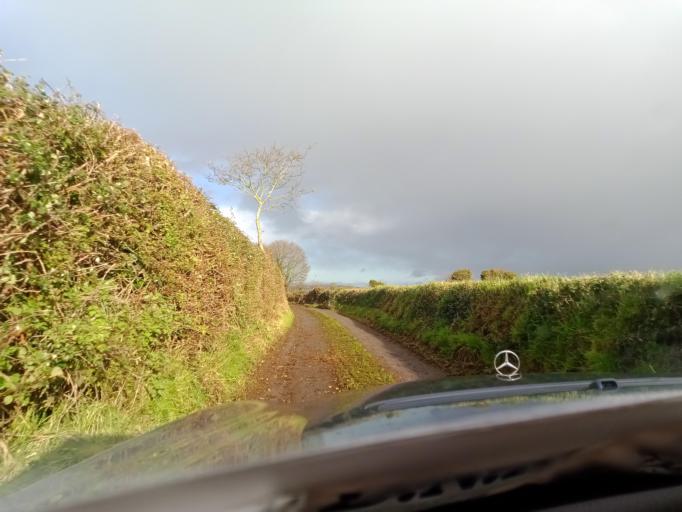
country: IE
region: Leinster
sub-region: Kilkenny
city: Mooncoin
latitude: 52.2960
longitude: -7.2716
